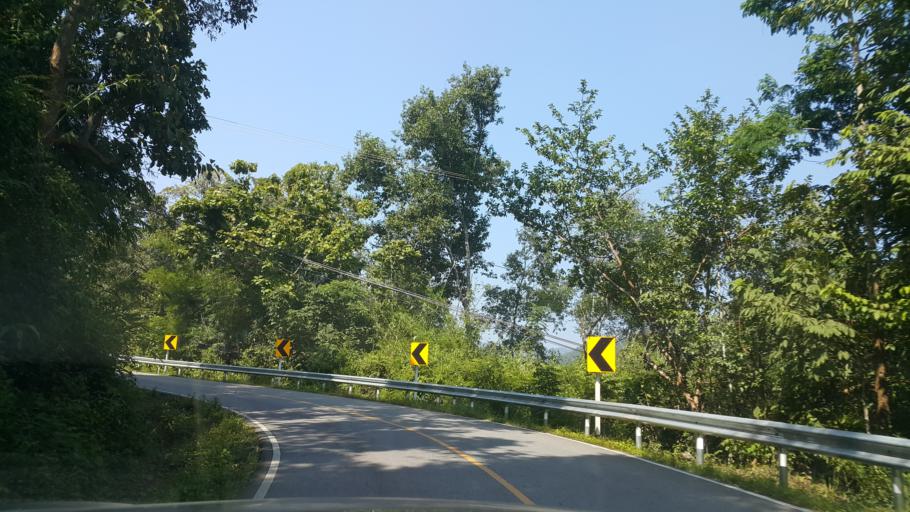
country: TH
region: Chiang Mai
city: Samoeng
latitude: 18.8653
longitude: 98.6323
